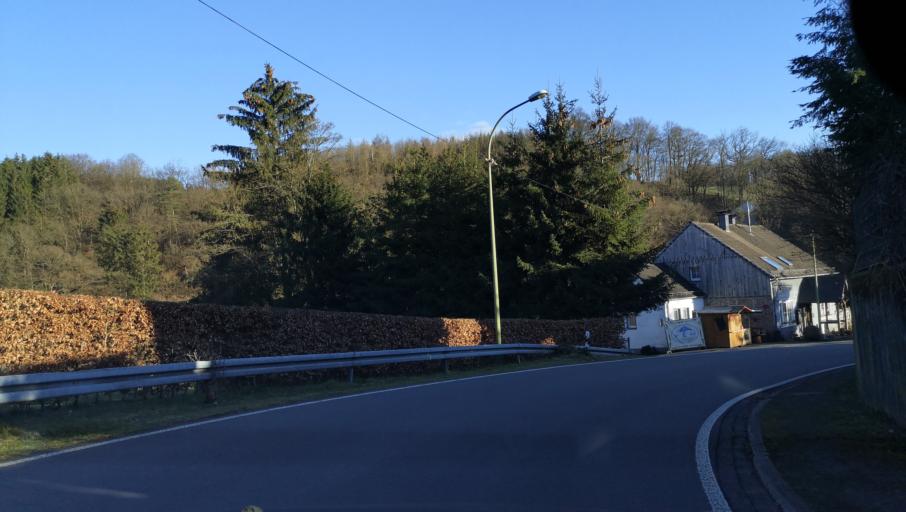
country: DE
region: North Rhine-Westphalia
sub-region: Regierungsbezirk Arnsberg
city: Breckerfeld
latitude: 51.2590
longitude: 7.4238
